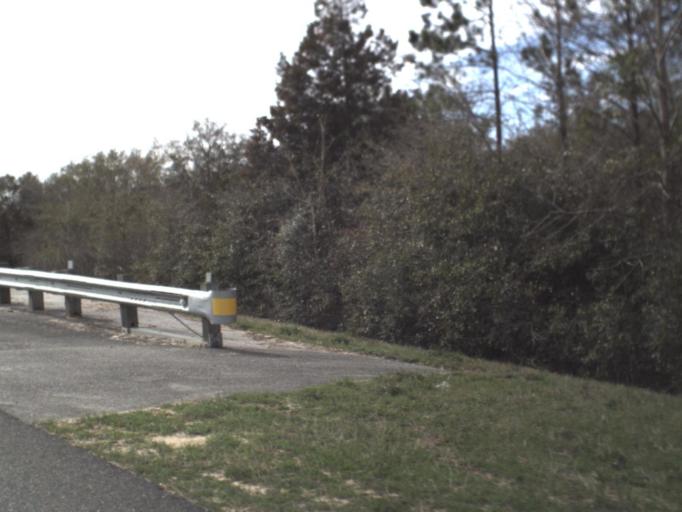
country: US
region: Florida
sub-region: Bay County
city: Youngstown
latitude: 30.5301
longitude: -85.3981
